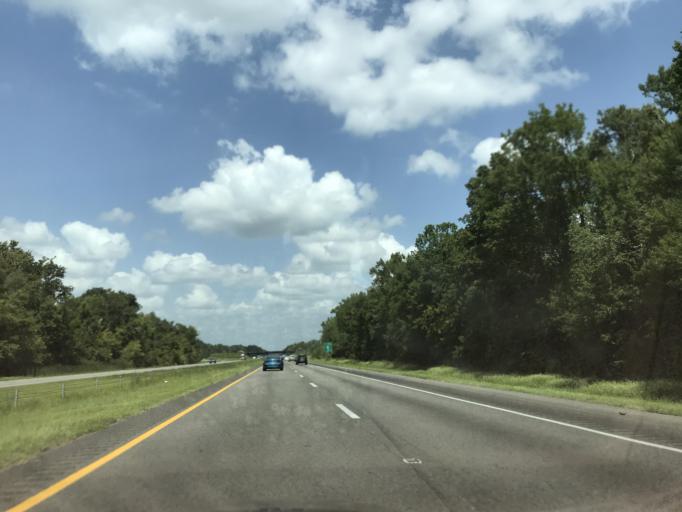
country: US
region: North Carolina
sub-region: Pender County
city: Rocky Point
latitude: 34.4347
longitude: -77.8725
